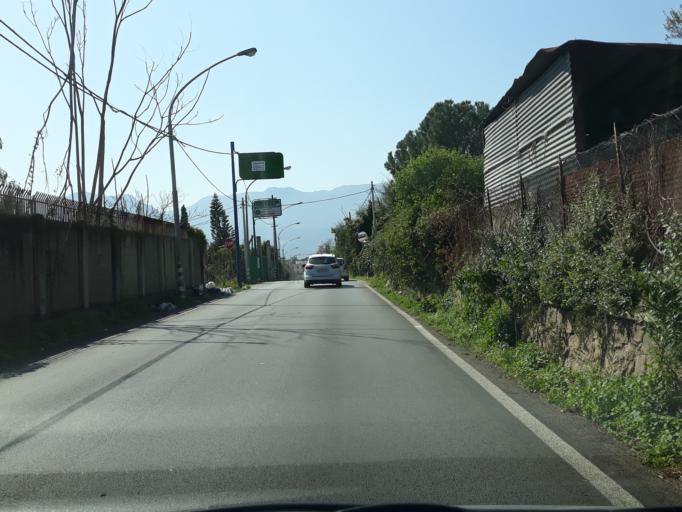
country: IT
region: Sicily
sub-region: Palermo
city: Monreale
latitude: 38.0997
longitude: 13.3100
